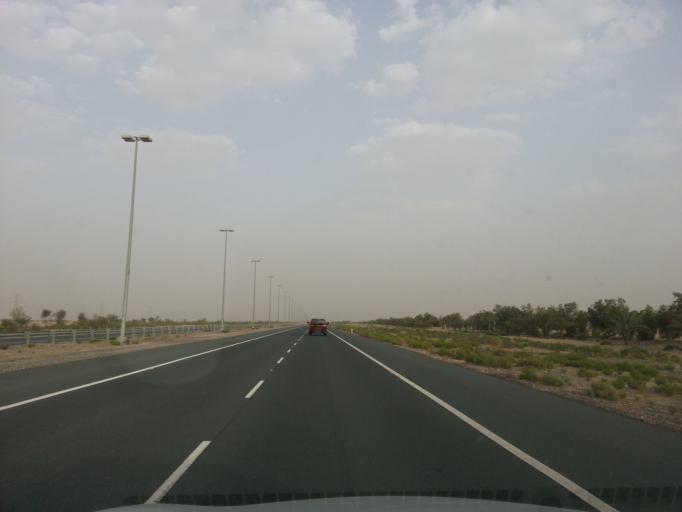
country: AE
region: Dubai
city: Dubai
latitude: 24.5940
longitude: 55.1409
